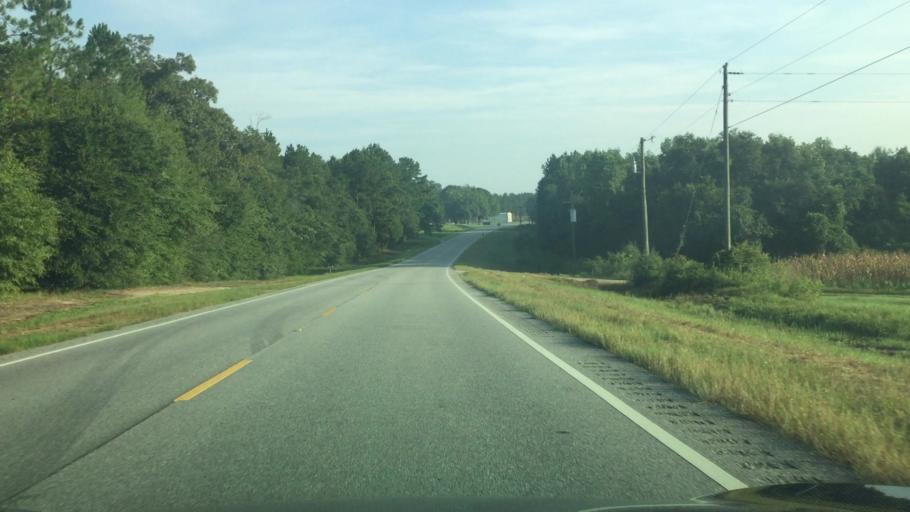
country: US
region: Alabama
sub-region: Covington County
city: Andalusia
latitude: 31.1360
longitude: -86.4593
